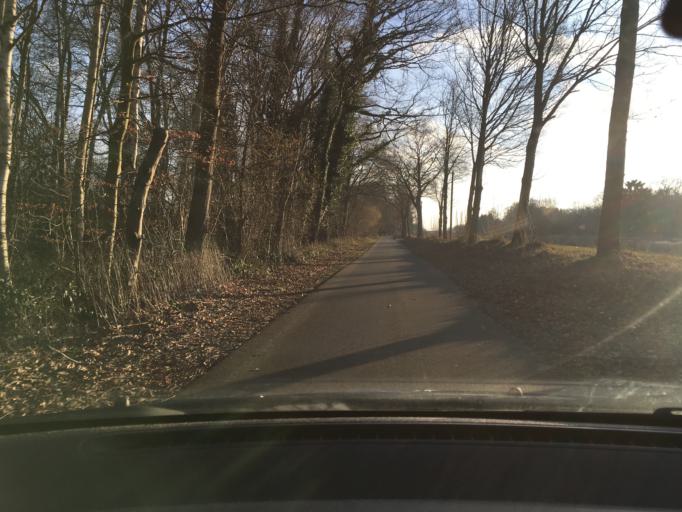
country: DE
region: Schleswig-Holstein
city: Witzeeze
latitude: 53.4579
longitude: 10.6261
